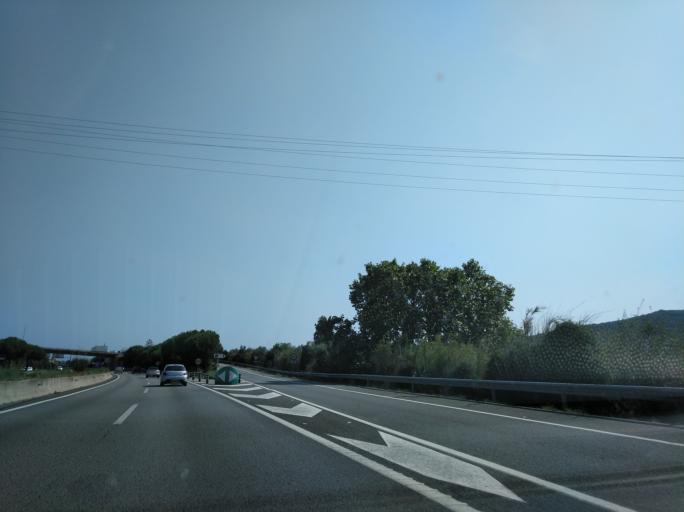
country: ES
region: Catalonia
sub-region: Provincia de Barcelona
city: Argentona
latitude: 41.5539
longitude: 2.4091
